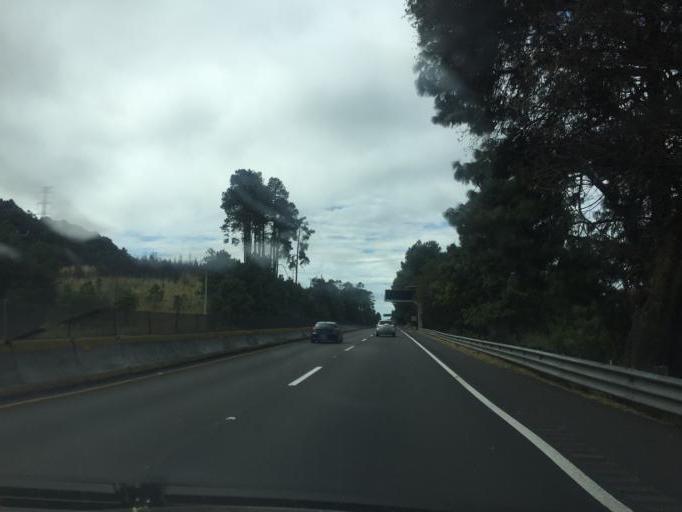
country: MX
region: Morelos
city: Tres Marias
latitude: 19.0801
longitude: -99.2326
